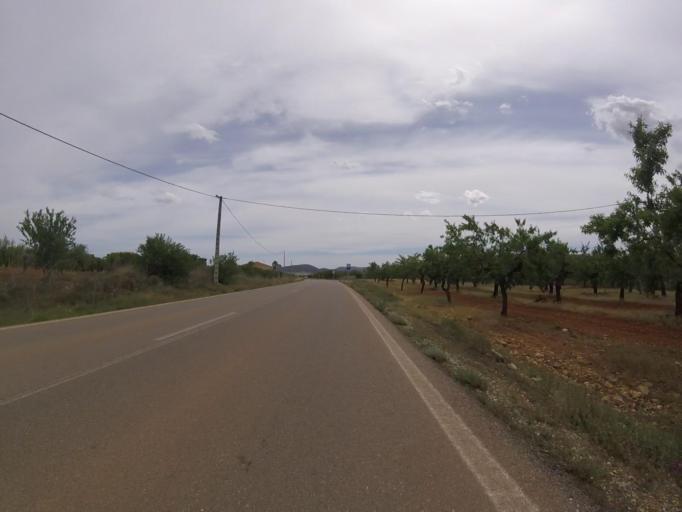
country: ES
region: Valencia
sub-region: Provincia de Castello
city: Cabanes
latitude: 40.1680
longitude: 0.0031
